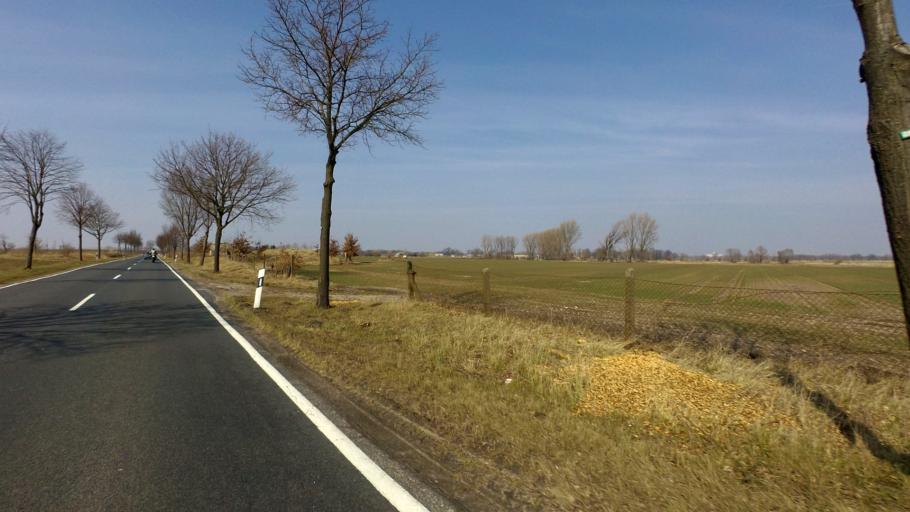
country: DE
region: Brandenburg
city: Ketzin
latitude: 52.4471
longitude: 12.8444
